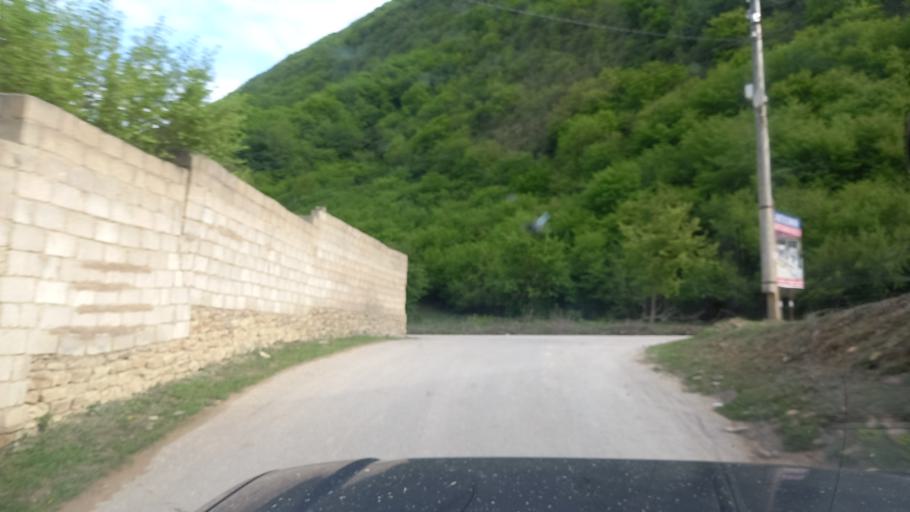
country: RU
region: Dagestan
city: Khuchni
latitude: 41.9712
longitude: 47.9310
